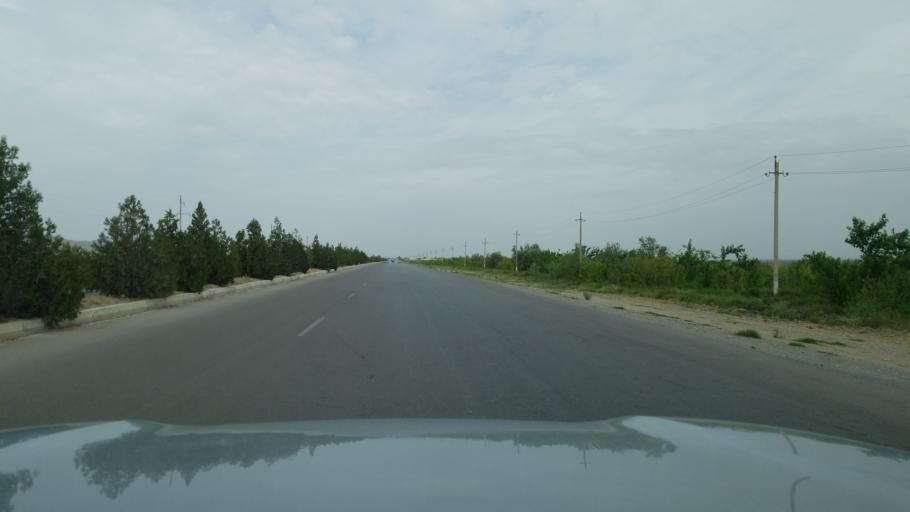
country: TM
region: Ahal
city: Arcabil
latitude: 38.2034
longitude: 57.8229
